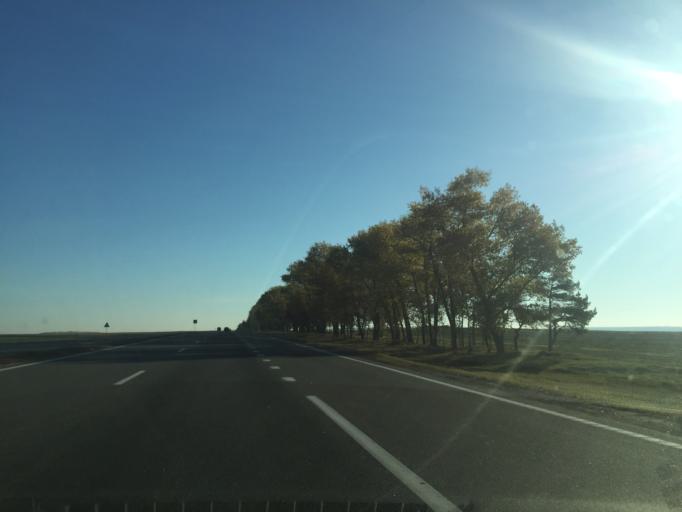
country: BY
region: Minsk
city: Smilavichy
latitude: 53.7603
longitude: 28.0455
